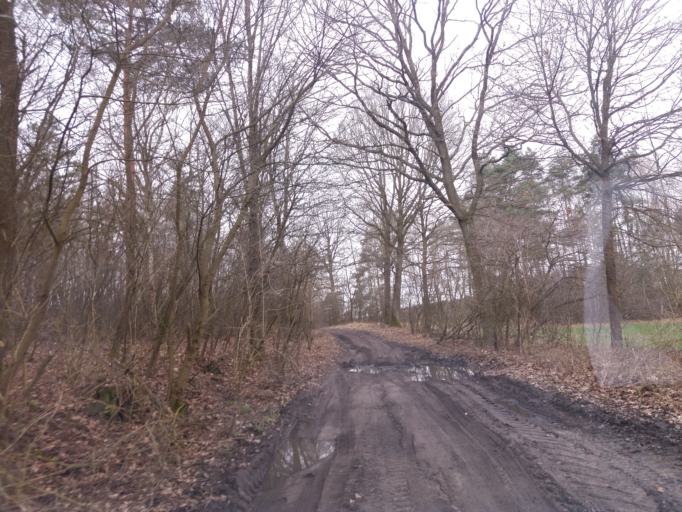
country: PL
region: West Pomeranian Voivodeship
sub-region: Powiat choszczenski
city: Bierzwnik
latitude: 53.1465
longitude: 15.6098
